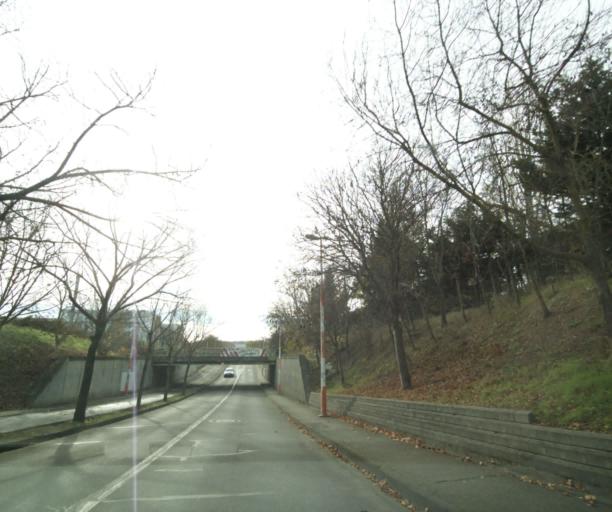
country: FR
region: Midi-Pyrenees
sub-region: Departement de la Haute-Garonne
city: Ramonville-Saint-Agne
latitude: 43.5790
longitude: 1.4726
